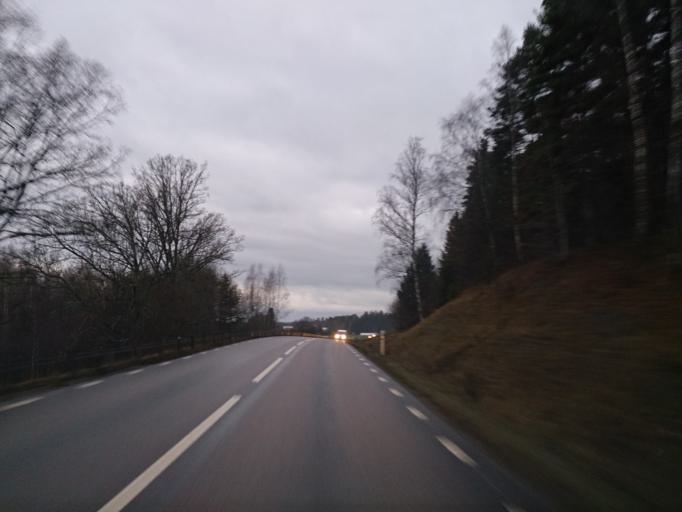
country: SE
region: OEstergoetland
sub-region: Atvidabergs Kommun
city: Atvidaberg
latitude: 58.2803
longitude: 15.9055
